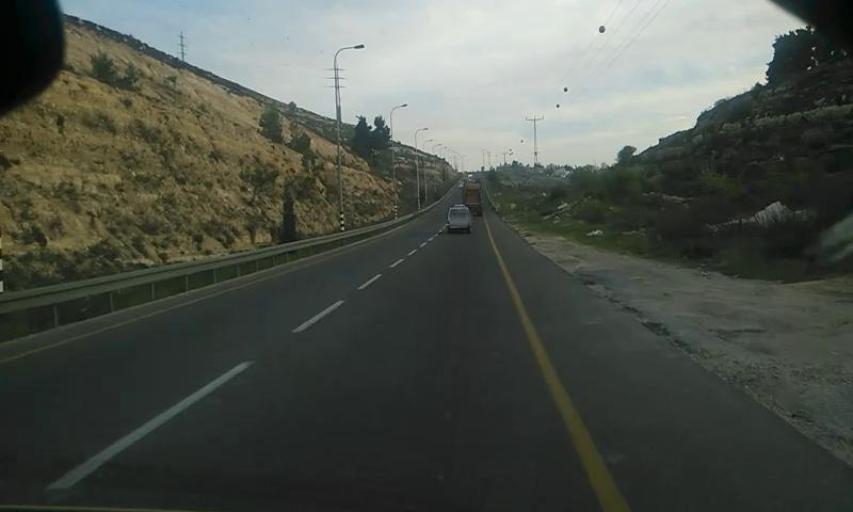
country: PS
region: West Bank
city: Halhul
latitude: 31.5909
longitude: 35.1162
